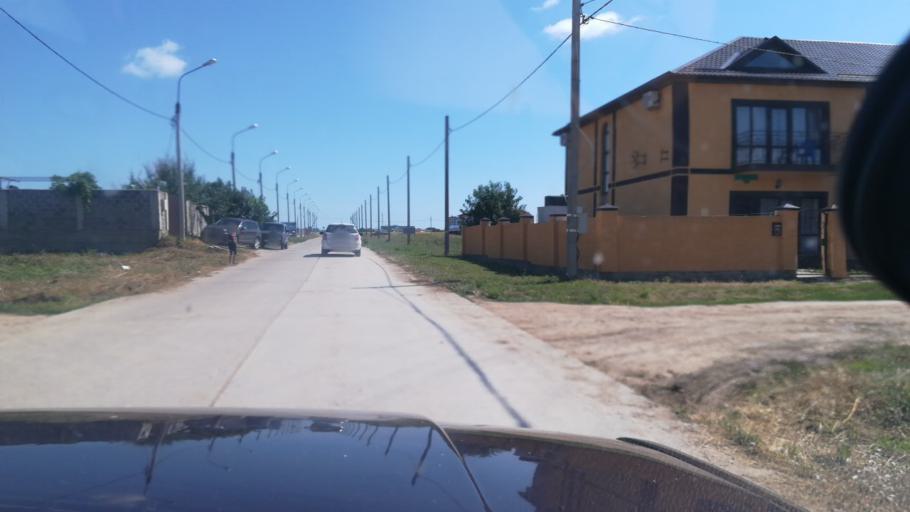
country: RU
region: Krasnodarskiy
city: Vityazevo
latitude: 44.9910
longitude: 37.2755
